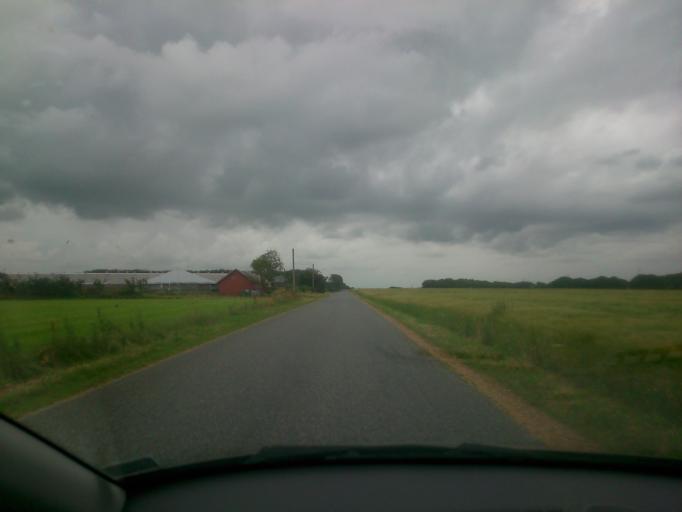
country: DK
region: South Denmark
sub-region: Esbjerg Kommune
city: Esbjerg
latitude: 55.5477
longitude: 8.4549
